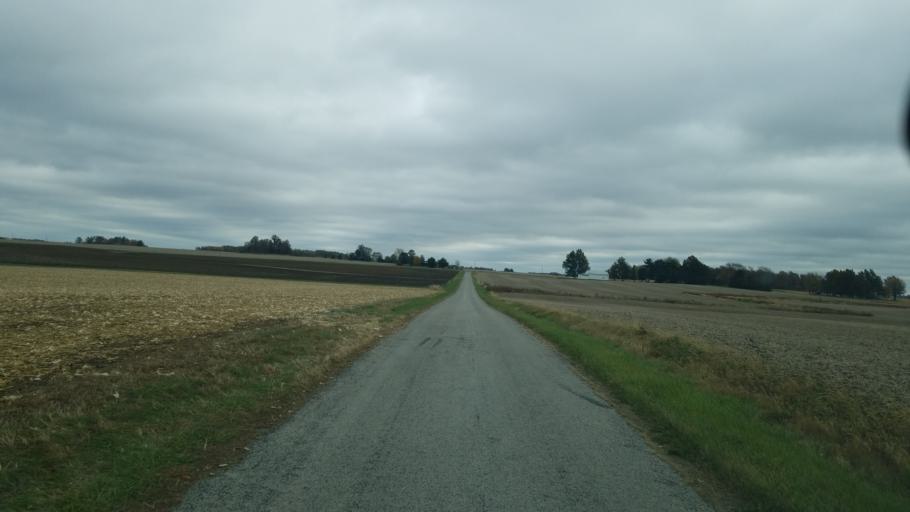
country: US
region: Ohio
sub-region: Crawford County
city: Bucyrus
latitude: 40.9073
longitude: -82.8616
